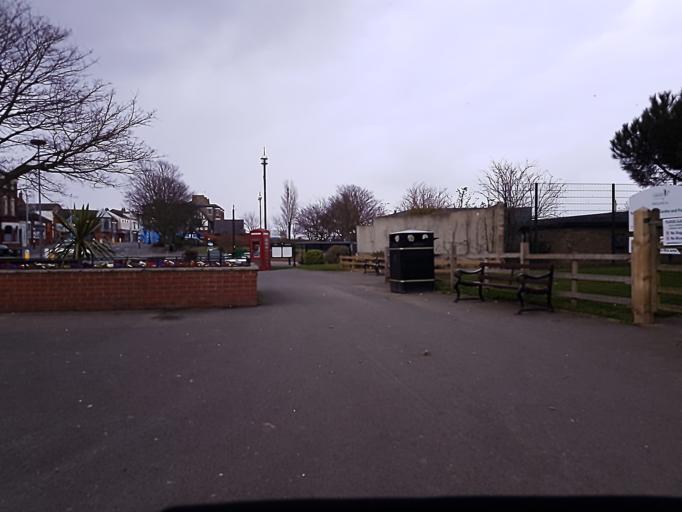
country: GB
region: England
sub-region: North East Lincolnshire
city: Cleethorpes
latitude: 53.5603
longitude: -0.0281
